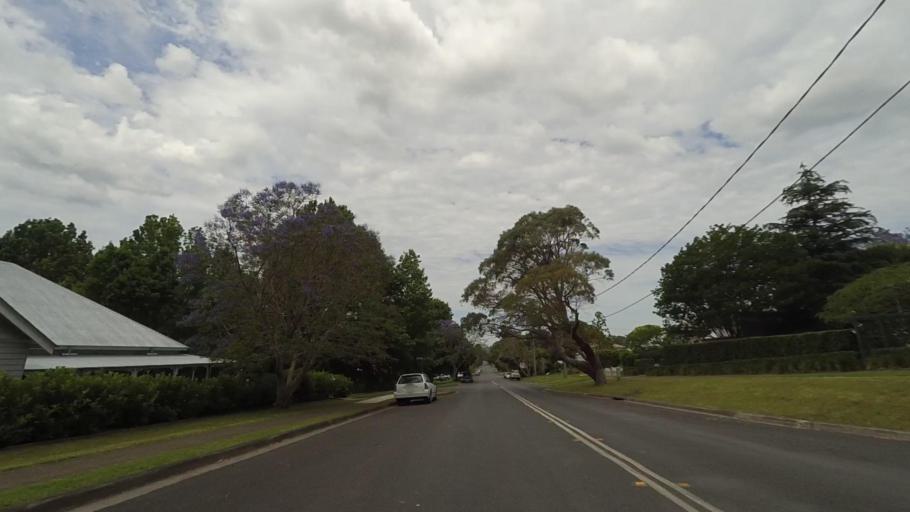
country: AU
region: New South Wales
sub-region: Shoalhaven Shire
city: Berry
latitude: -34.7767
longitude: 150.6910
